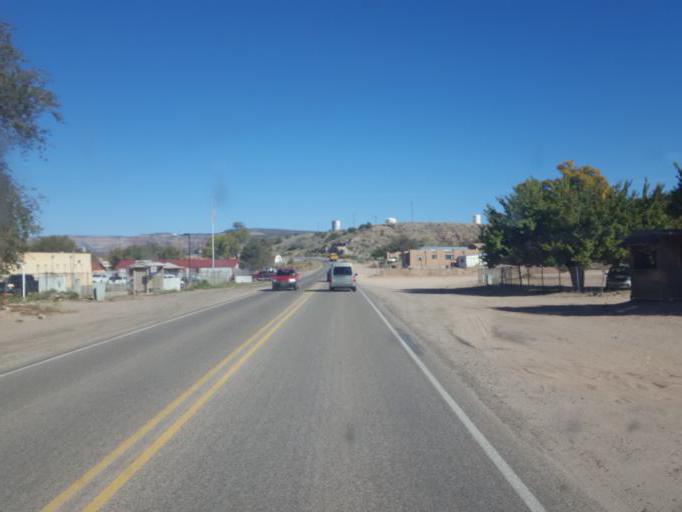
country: US
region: New Mexico
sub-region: Sandoval County
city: Jemez Pueblo
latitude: 35.6069
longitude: -106.7265
